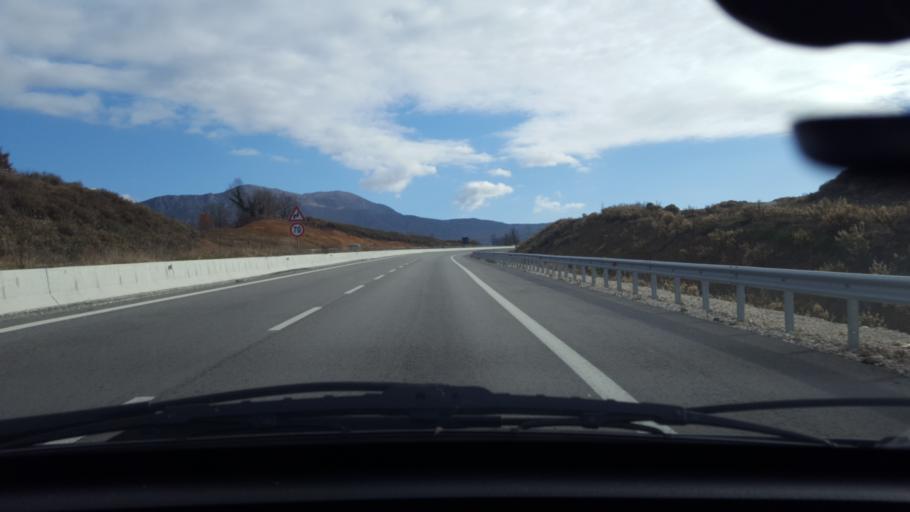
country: AL
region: Tirane
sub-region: Rrethi i Tiranes
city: Krrabe
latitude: 41.2254
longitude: 19.9398
